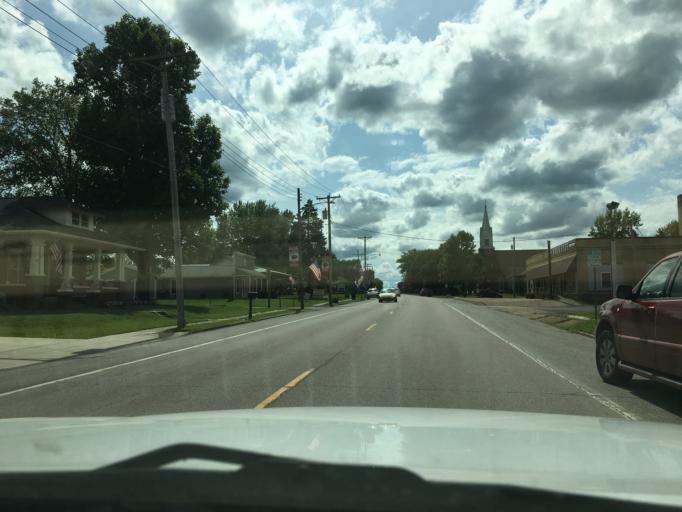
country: US
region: Missouri
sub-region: Franklin County
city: Gerald
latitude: 38.3872
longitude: -91.4006
